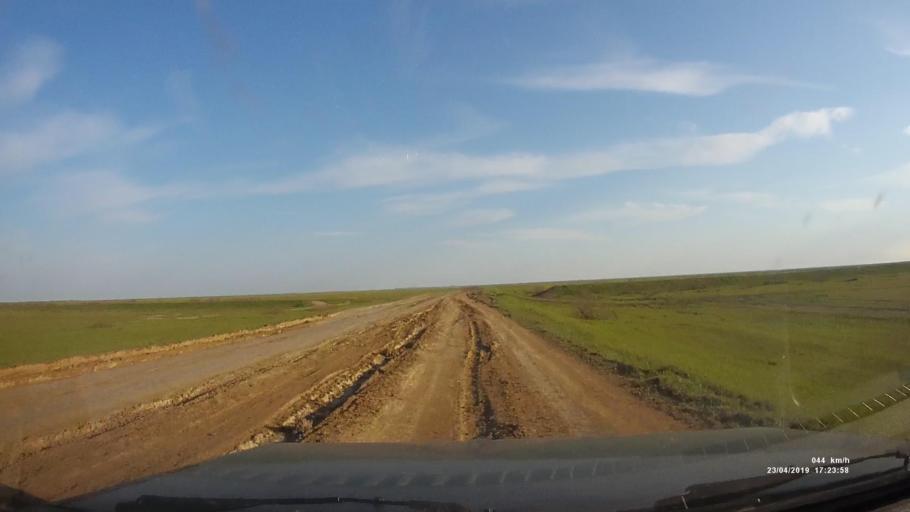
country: RU
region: Kalmykiya
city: Priyutnoye
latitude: 46.1591
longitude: 43.5081
